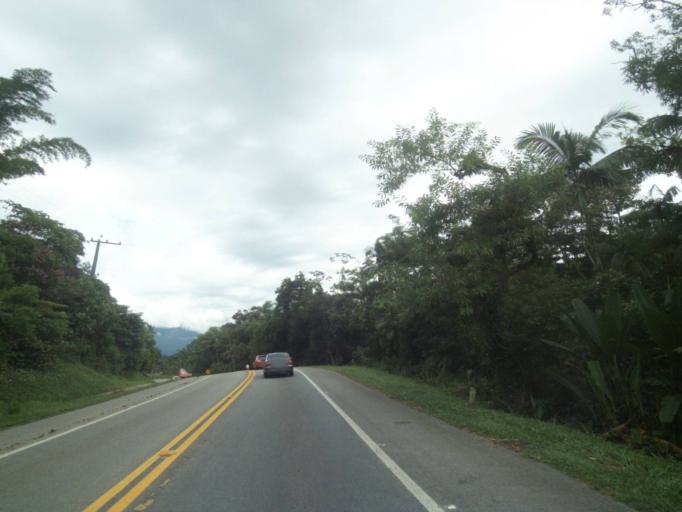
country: BR
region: Parana
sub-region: Antonina
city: Antonina
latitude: -25.5123
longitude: -48.8084
